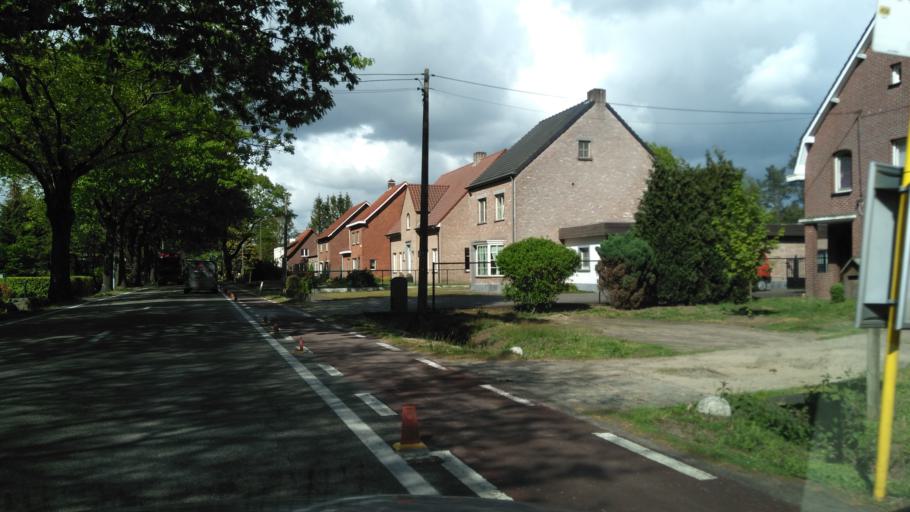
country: NL
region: North Brabant
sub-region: Gemeente Goirle
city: Goirle
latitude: 51.4590
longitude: 5.0432
